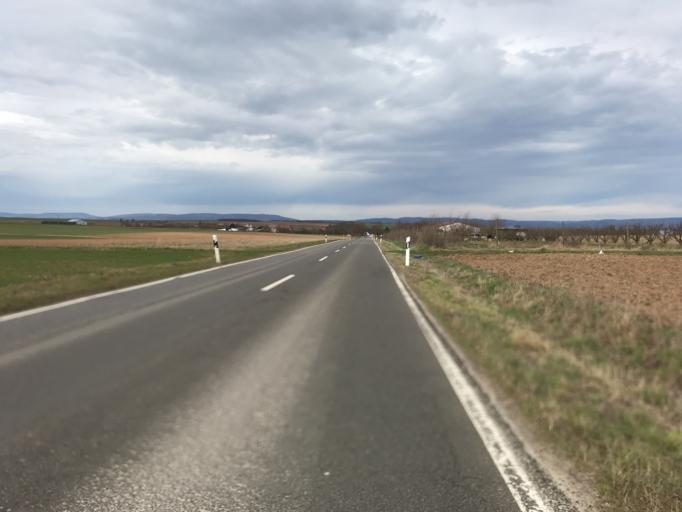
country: DE
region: Rheinland-Pfalz
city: Ober-Hilbersheim
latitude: 49.8925
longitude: 8.0359
